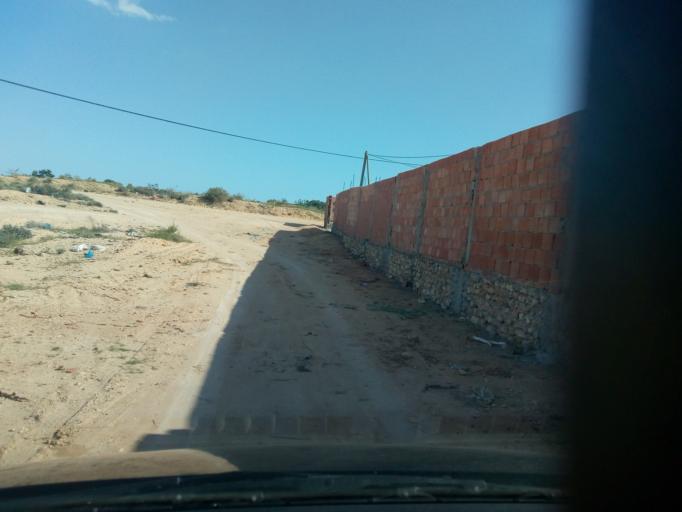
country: TN
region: Safaqis
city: Sfax
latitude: 34.7265
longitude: 10.6045
